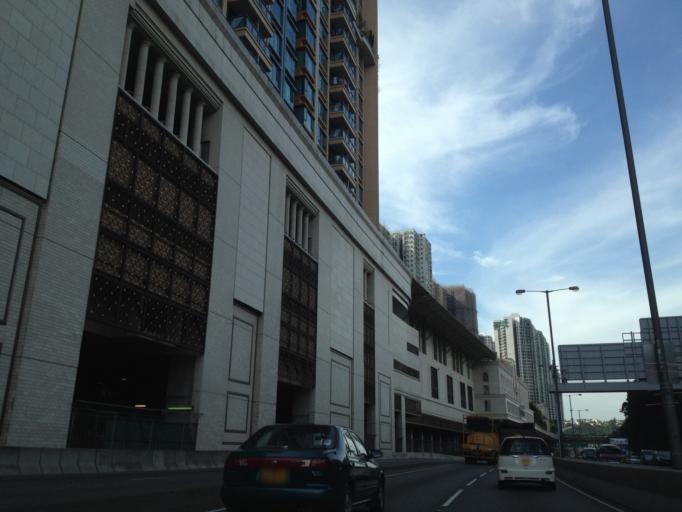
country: HK
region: Sha Tin
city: Sha Tin
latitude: 22.3943
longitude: 114.1992
